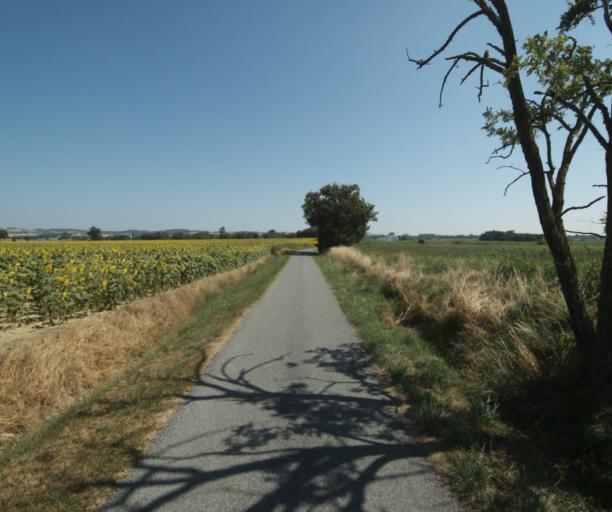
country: FR
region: Midi-Pyrenees
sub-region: Departement du Tarn
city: Puylaurens
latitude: 43.5228
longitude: 1.9541
